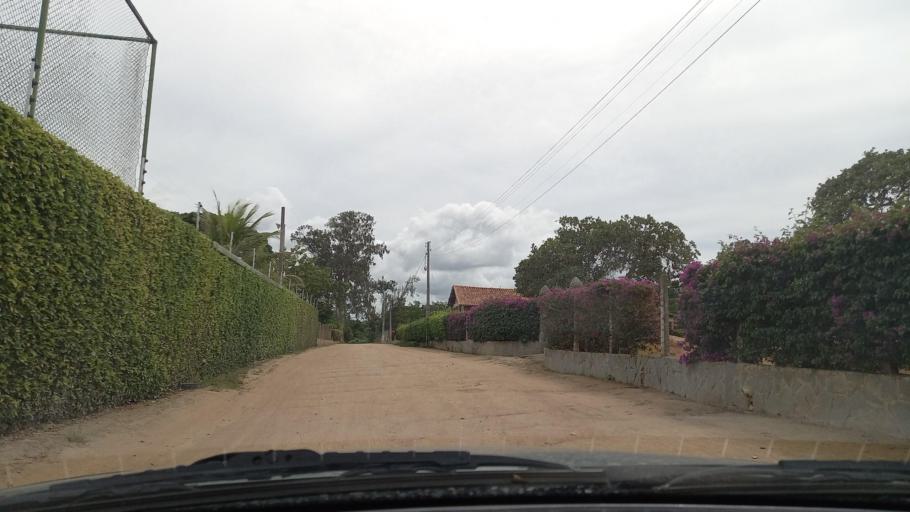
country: BR
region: Pernambuco
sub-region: Gravata
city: Gravata
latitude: -8.1918
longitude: -35.5991
